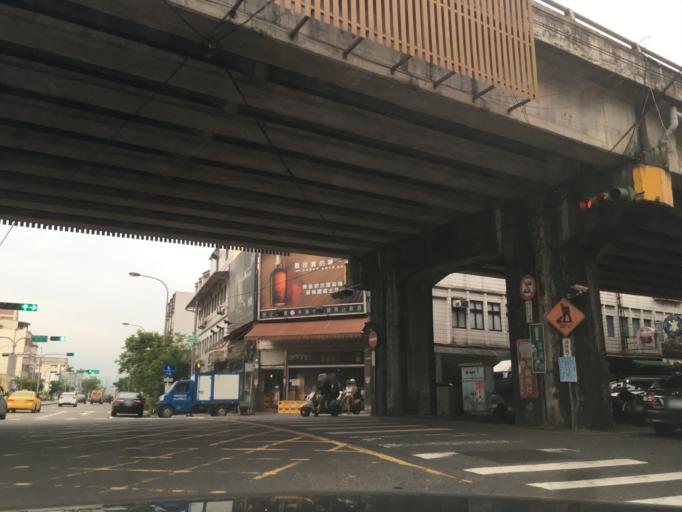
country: TW
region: Taiwan
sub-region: Yilan
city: Yilan
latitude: 24.7579
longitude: 121.7589
